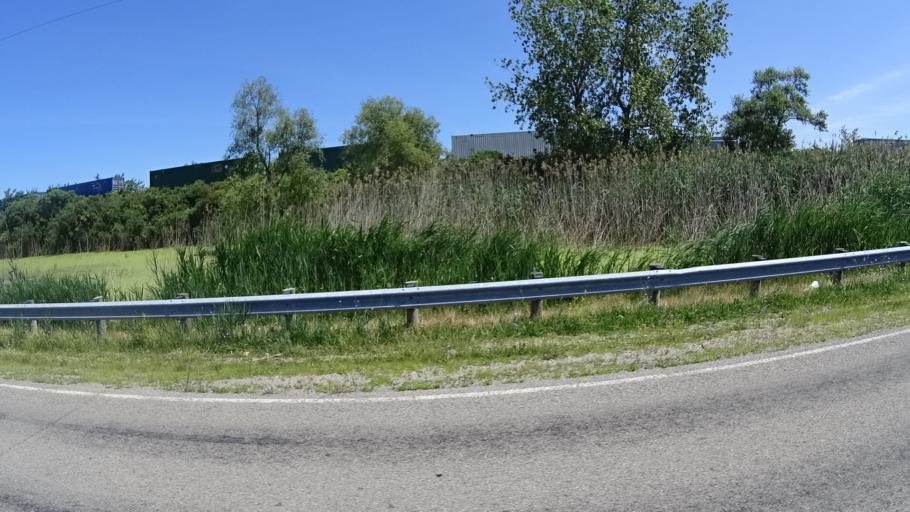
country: US
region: Ohio
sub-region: Erie County
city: Sandusky
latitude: 41.4663
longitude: -82.8044
